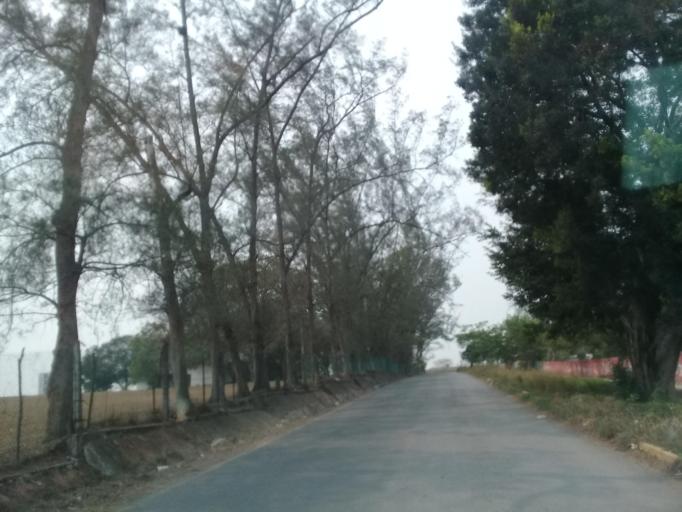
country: MX
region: Veracruz
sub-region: Medellin
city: La Laguna y Monte del Castillo
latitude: 18.9707
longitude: -96.1196
